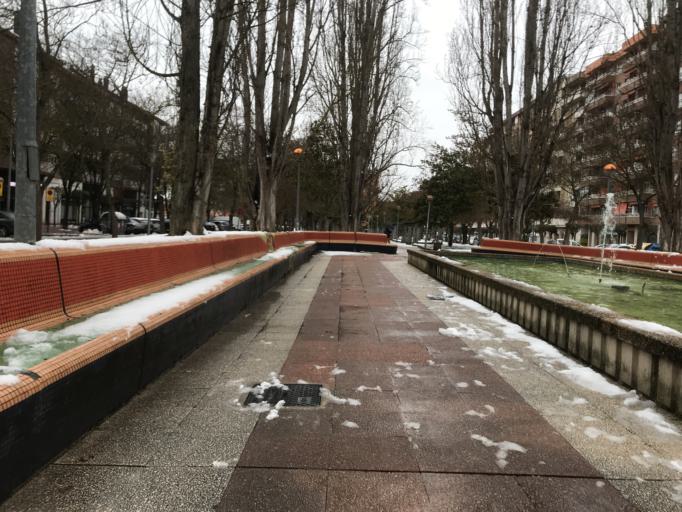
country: ES
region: Basque Country
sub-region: Provincia de Alava
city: Gasteiz / Vitoria
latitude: 42.8459
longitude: -2.6836
